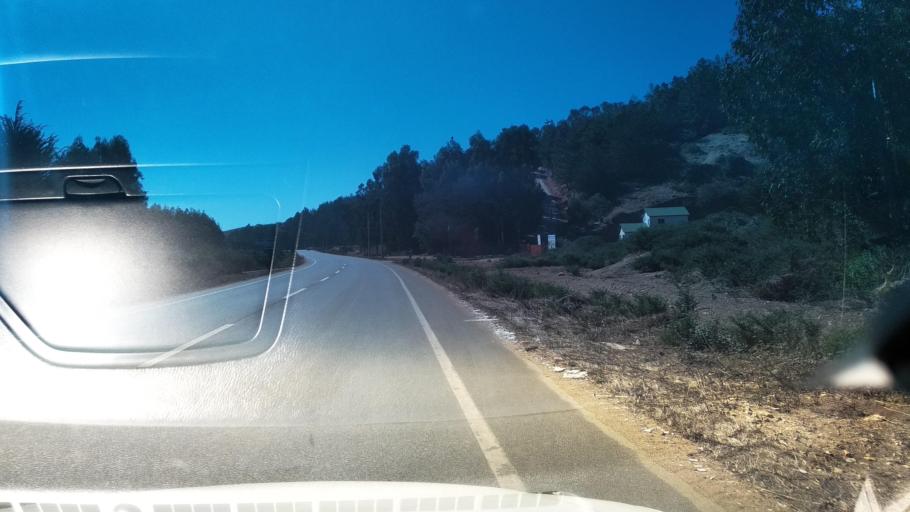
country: CL
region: O'Higgins
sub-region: Provincia de Colchagua
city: Santa Cruz
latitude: -34.4717
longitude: -72.0184
